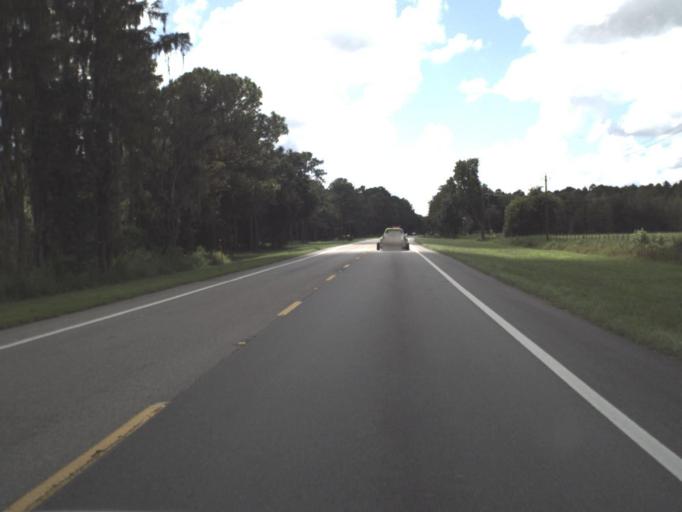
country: US
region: Florida
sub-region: Polk County
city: Polk City
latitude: 28.2428
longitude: -81.8212
